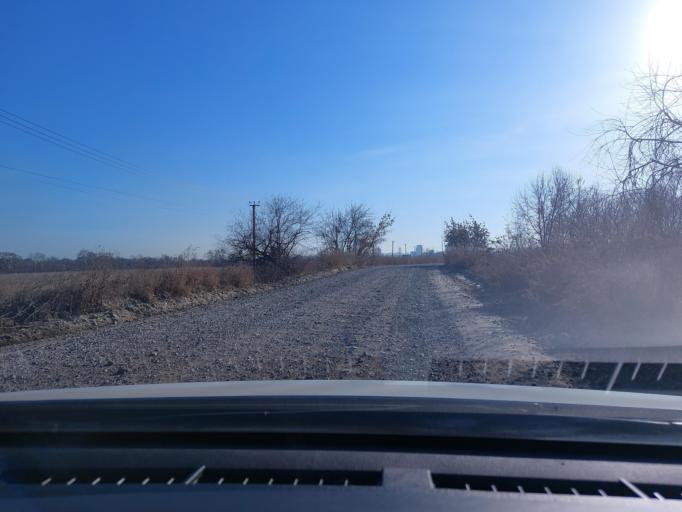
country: RU
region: Irkutsk
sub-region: Irkutskiy Rayon
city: Irkutsk
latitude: 52.3054
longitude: 104.2753
